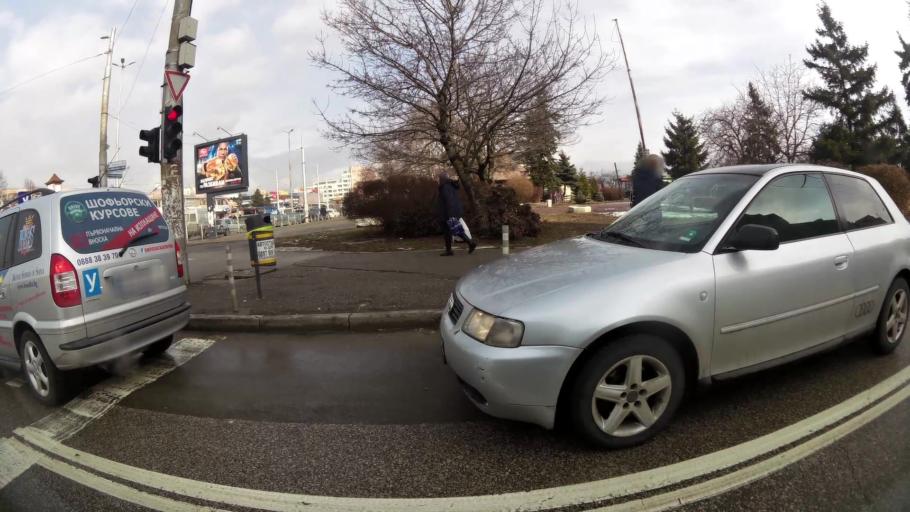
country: BG
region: Sofiya
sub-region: Obshtina Bozhurishte
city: Bozhurishte
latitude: 42.7158
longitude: 23.2514
